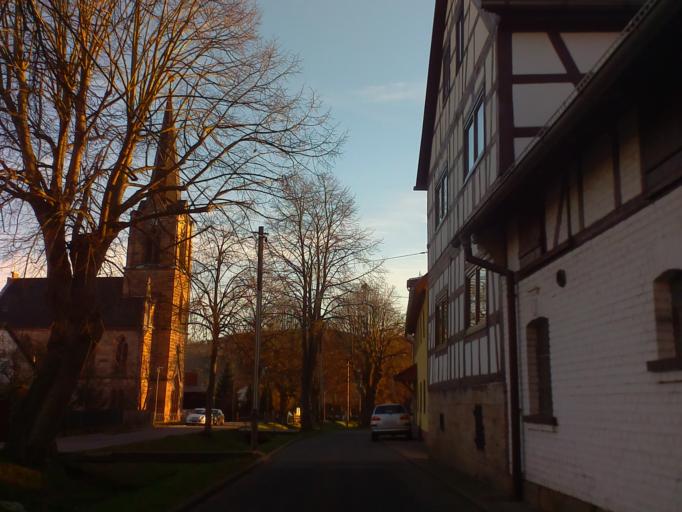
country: DE
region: Thuringia
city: Reinstadt
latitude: 50.7370
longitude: 11.4307
